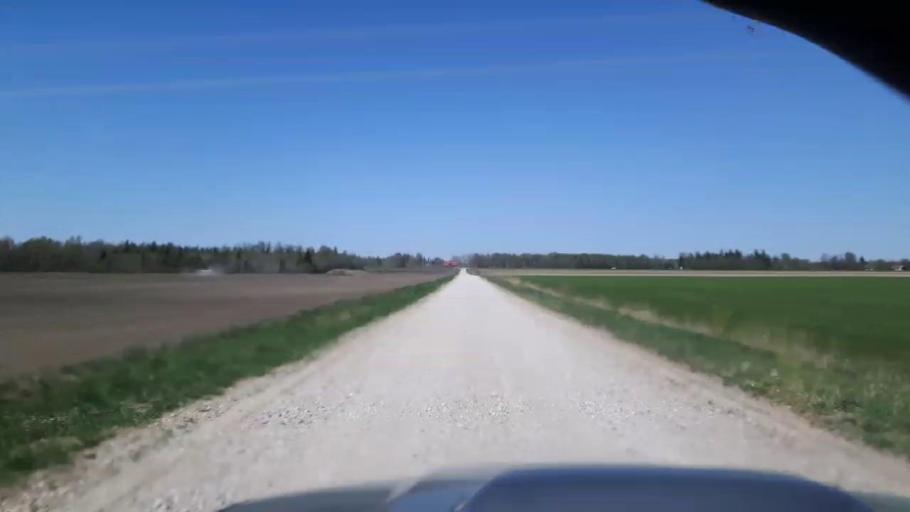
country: EE
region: Paernumaa
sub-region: Sindi linn
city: Sindi
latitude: 58.4778
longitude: 24.7442
